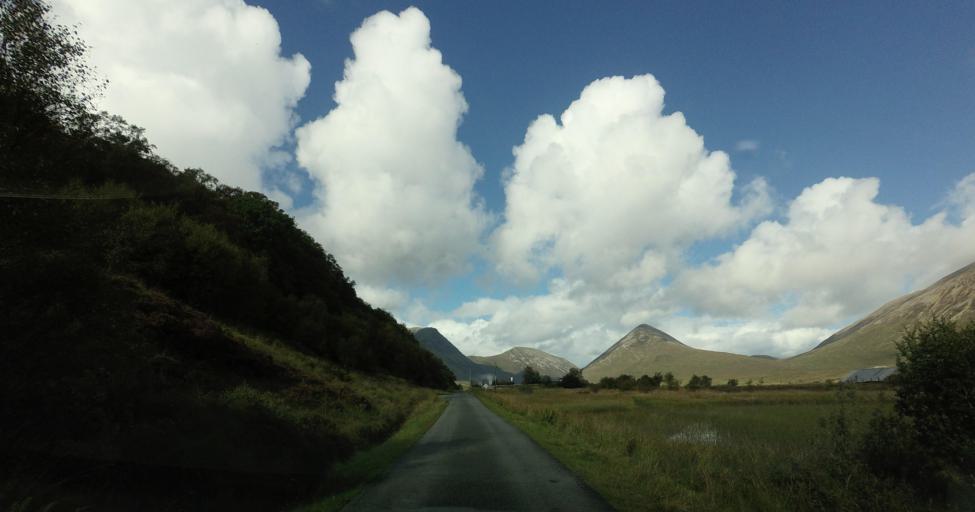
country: GB
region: Scotland
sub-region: Highland
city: Portree
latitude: 57.2070
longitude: -6.0297
